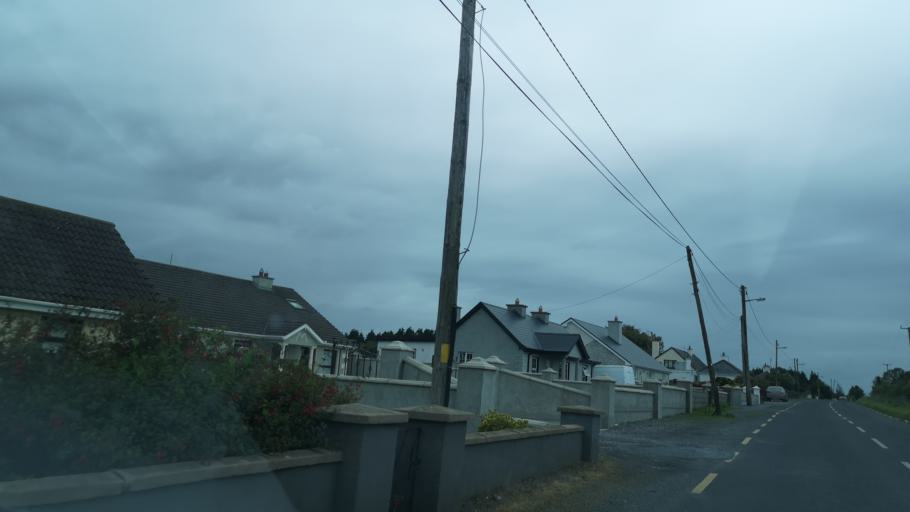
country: IE
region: Leinster
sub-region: Uibh Fhaili
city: Banagher
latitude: 53.1979
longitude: -7.9698
